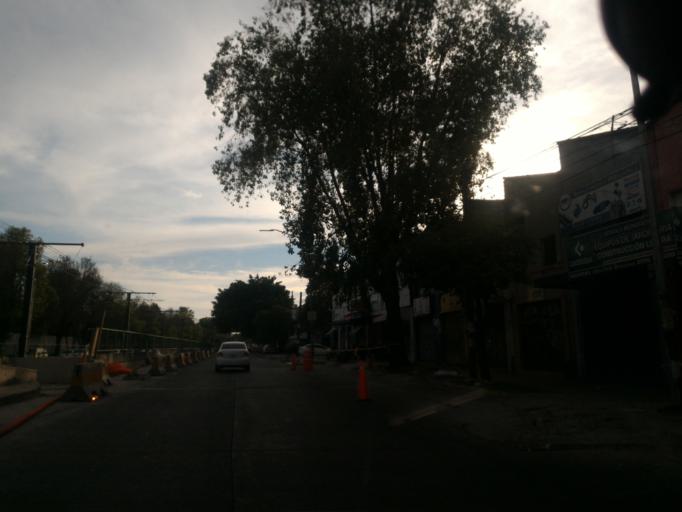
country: MX
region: Jalisco
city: Guadalajara
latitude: 20.6469
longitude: -103.3697
